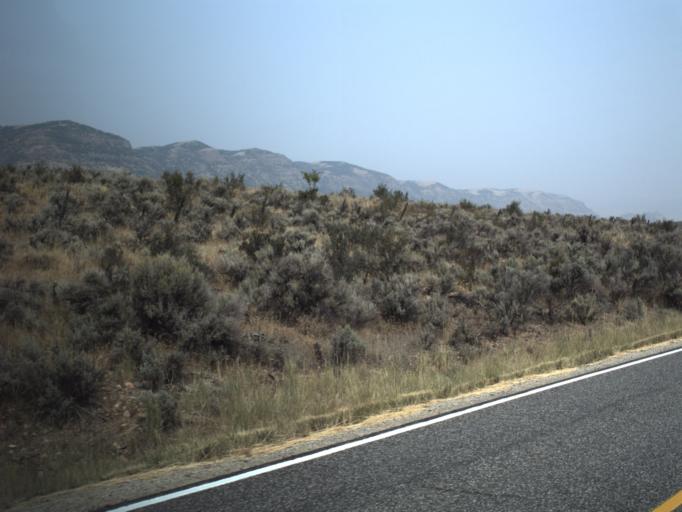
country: US
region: Utah
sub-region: Summit County
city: Coalville
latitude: 40.9742
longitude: -111.5380
